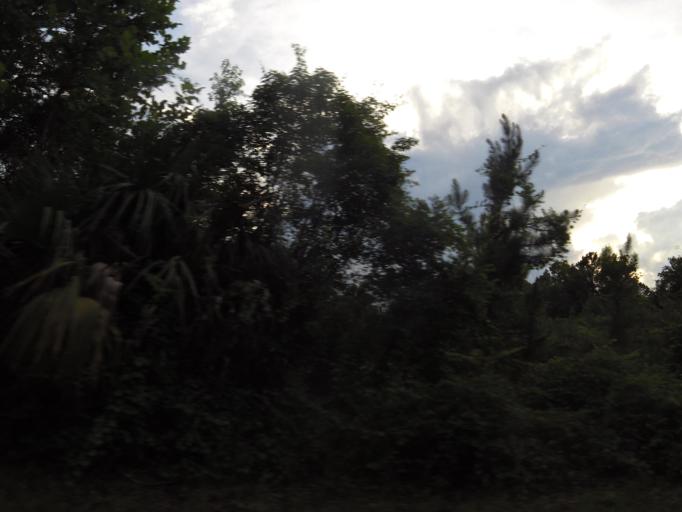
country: US
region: Florida
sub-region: Duval County
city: Jacksonville
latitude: 30.3386
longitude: -81.7899
